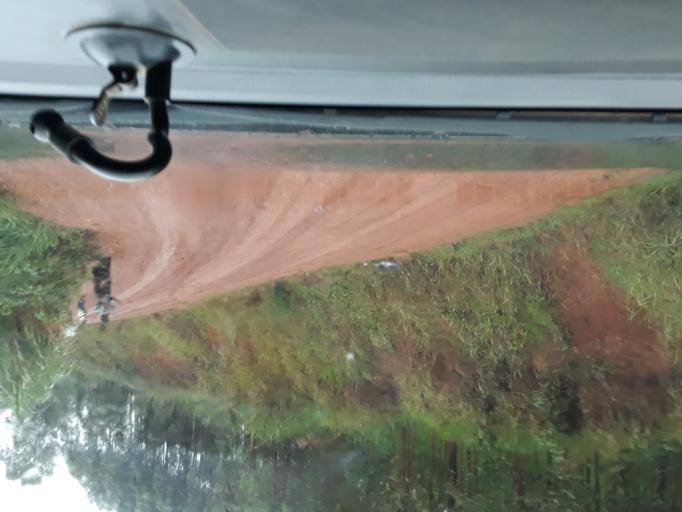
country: CD
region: Eastern Province
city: Bunia
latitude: 1.7504
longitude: 30.3525
